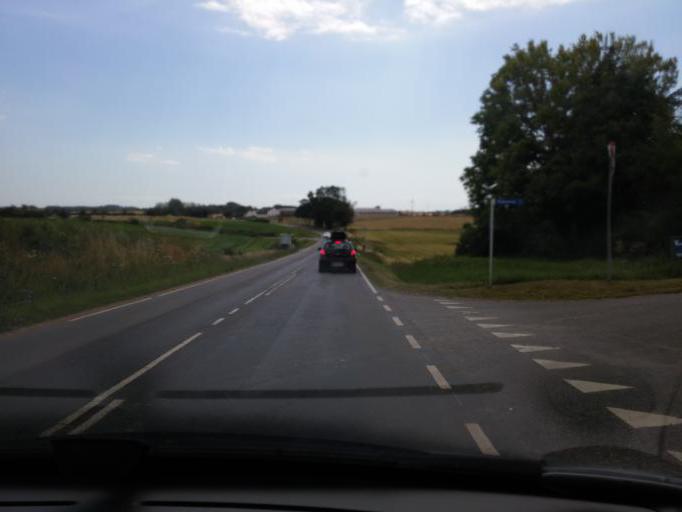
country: DK
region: South Denmark
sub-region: Langeland Kommune
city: Rudkobing
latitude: 54.8883
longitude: 10.7330
